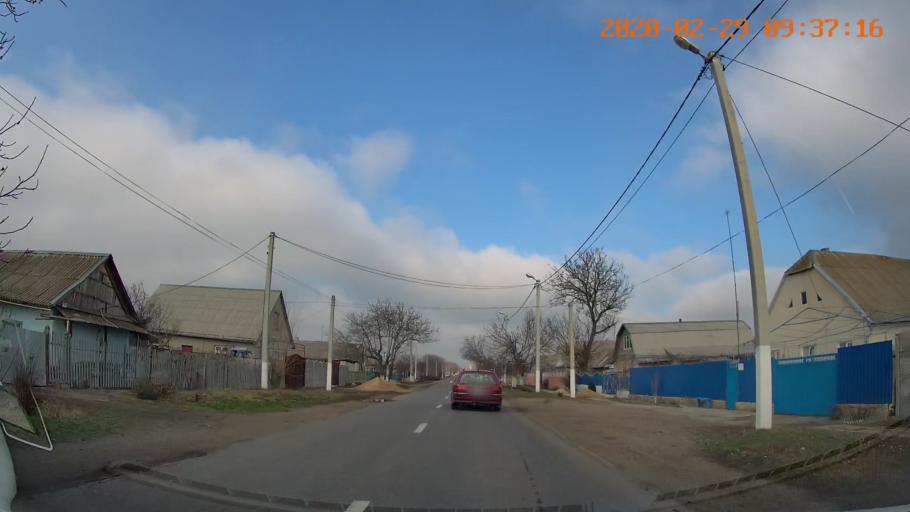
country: MD
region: Telenesti
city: Dnestrovsc
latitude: 46.6273
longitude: 29.8780
